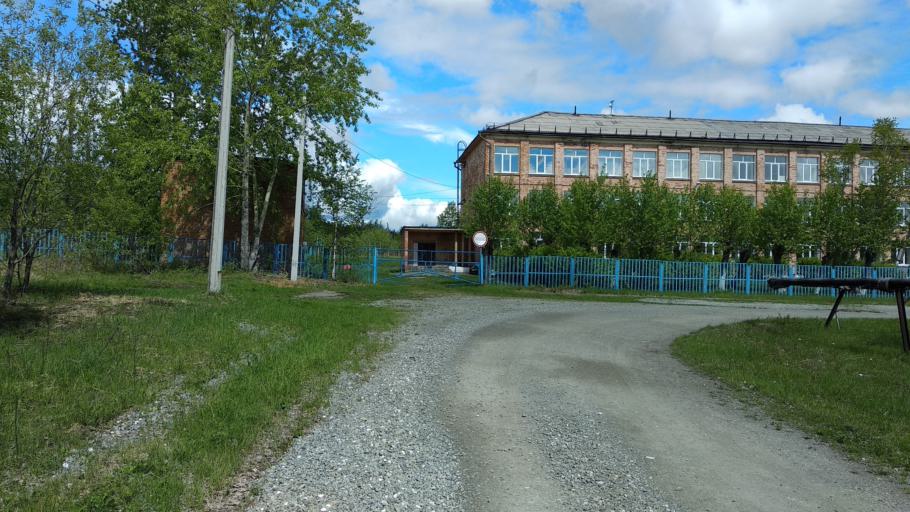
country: RU
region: Sverdlovsk
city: Krasnotur'insk
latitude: 59.7866
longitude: 60.1540
